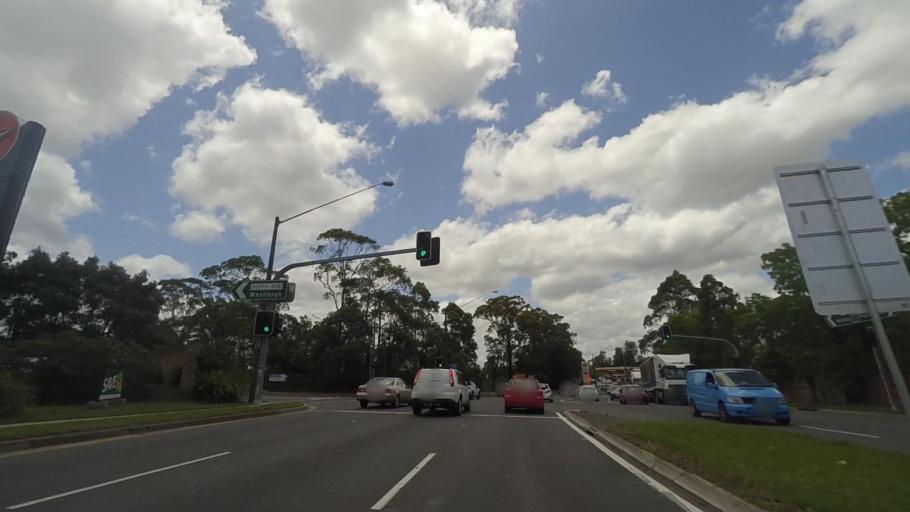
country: AU
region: New South Wales
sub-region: Hornsby Shire
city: Pennant Hills
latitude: -33.7266
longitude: 151.0840
